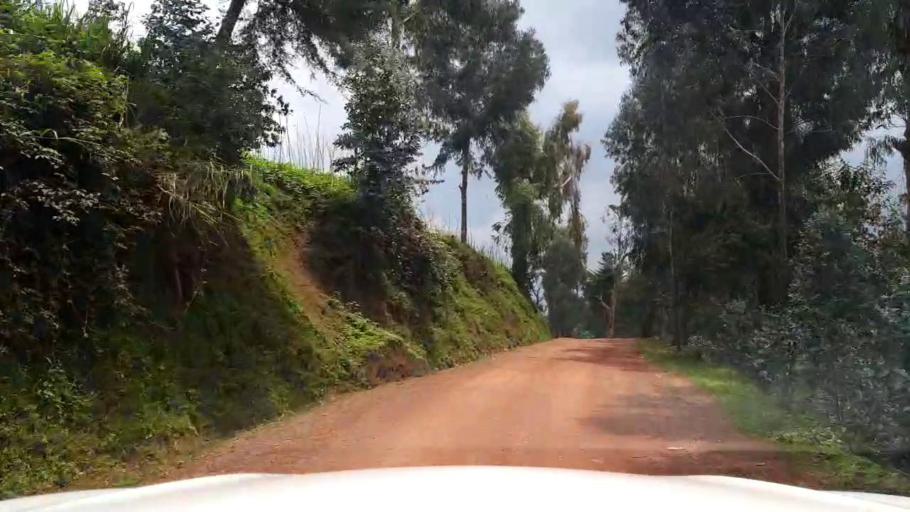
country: RW
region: Northern Province
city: Byumba
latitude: -1.5121
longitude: 29.9415
